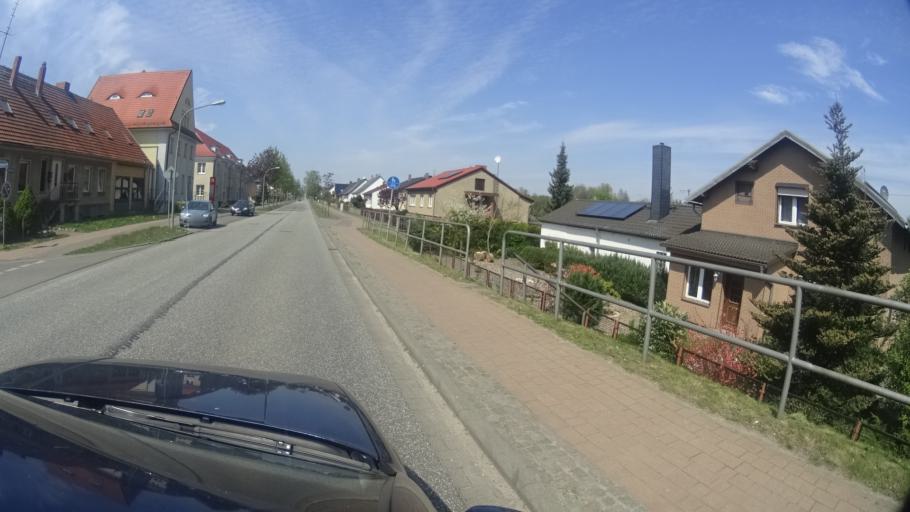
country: DE
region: Brandenburg
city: Wusterhausen
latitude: 52.8553
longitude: 12.4454
